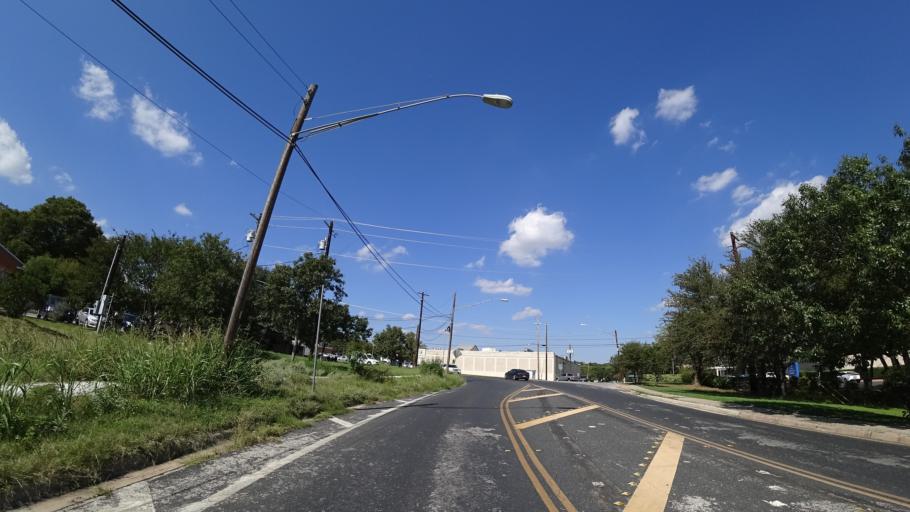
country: US
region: Texas
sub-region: Travis County
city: Austin
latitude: 30.3054
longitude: -97.7493
